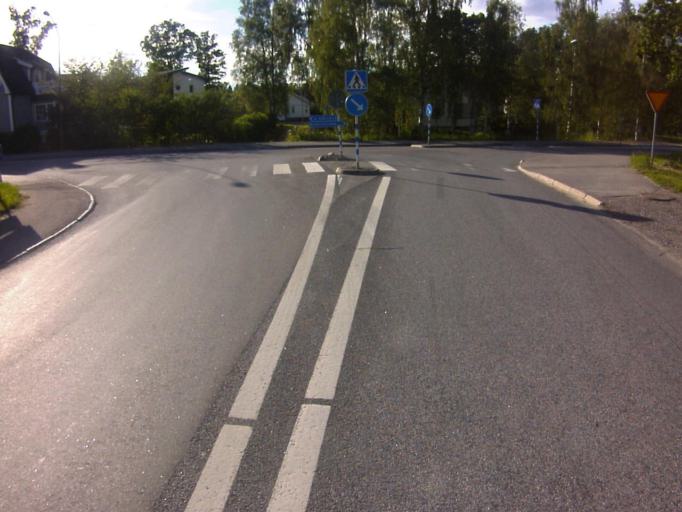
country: SE
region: Soedermanland
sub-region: Eskilstuna Kommun
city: Skogstorp
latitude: 59.3249
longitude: 16.4830
